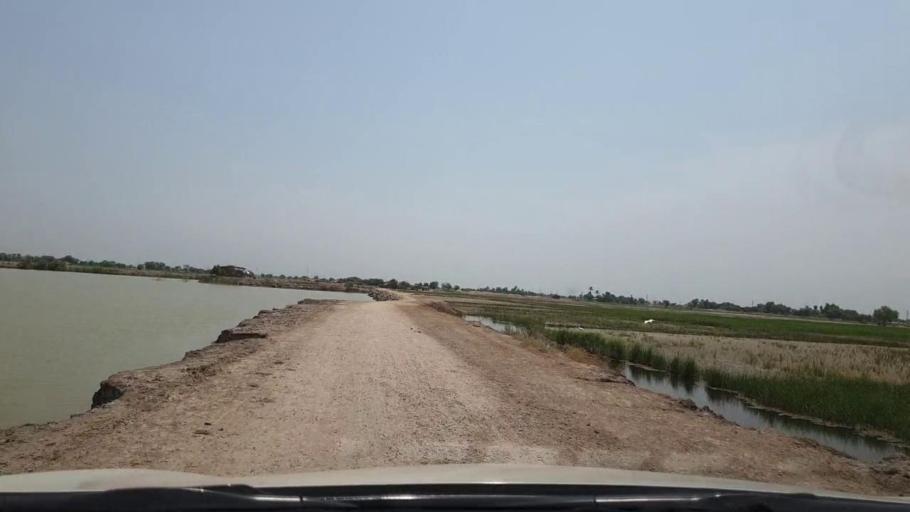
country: PK
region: Sindh
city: Ratodero
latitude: 27.8079
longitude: 68.2450
